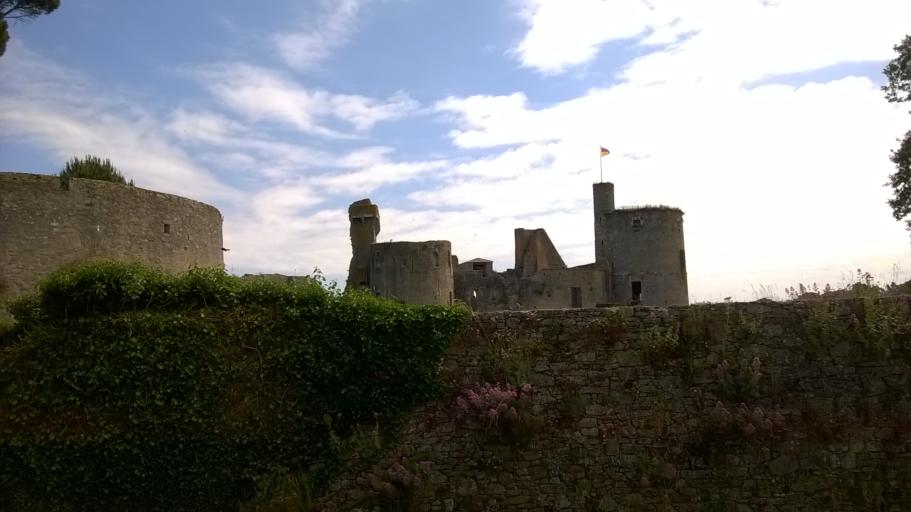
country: FR
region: Pays de la Loire
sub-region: Departement de la Loire-Atlantique
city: Clisson
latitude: 47.0860
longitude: -1.2820
